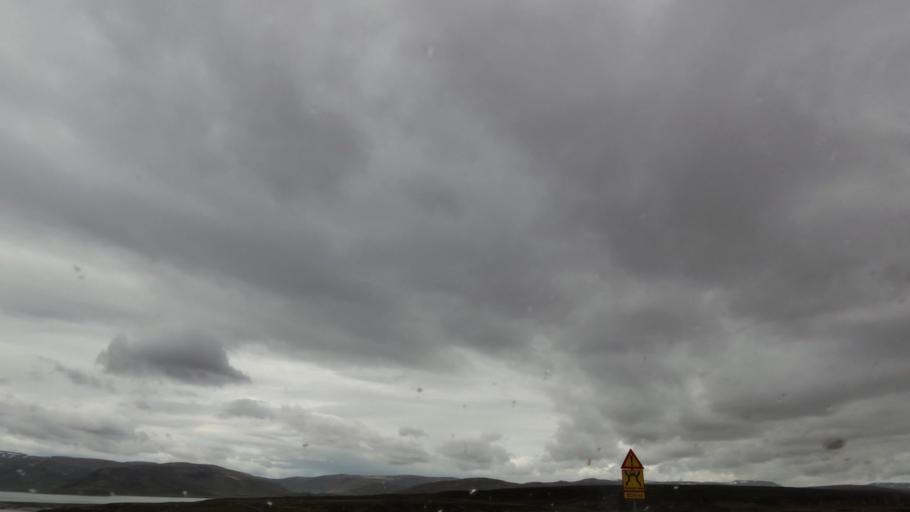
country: IS
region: West
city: Borgarnes
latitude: 65.1691
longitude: -21.7022
